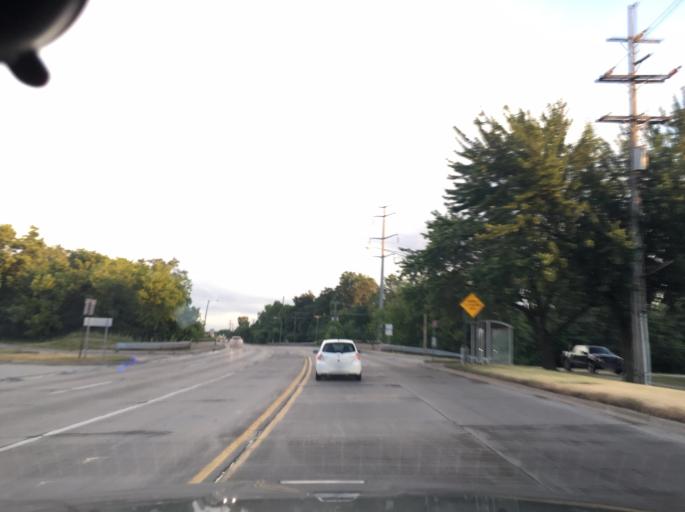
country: US
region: Michigan
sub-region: Macomb County
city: Clinton
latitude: 42.5789
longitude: -82.9521
